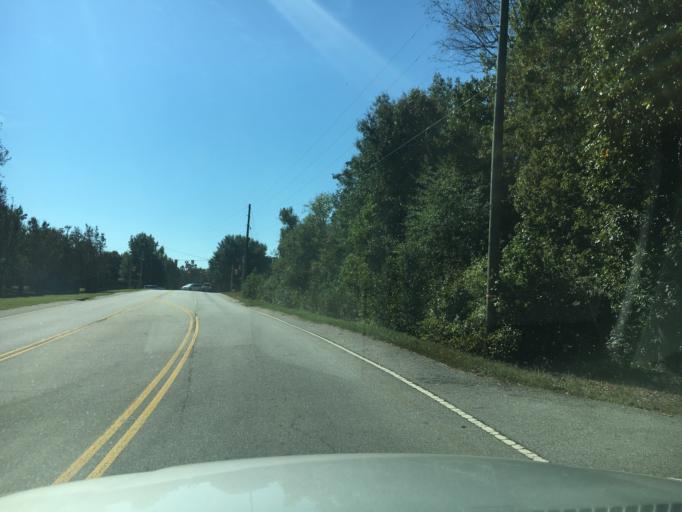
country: US
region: South Carolina
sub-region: Greenville County
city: Taylors
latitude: 34.8717
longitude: -82.2833
